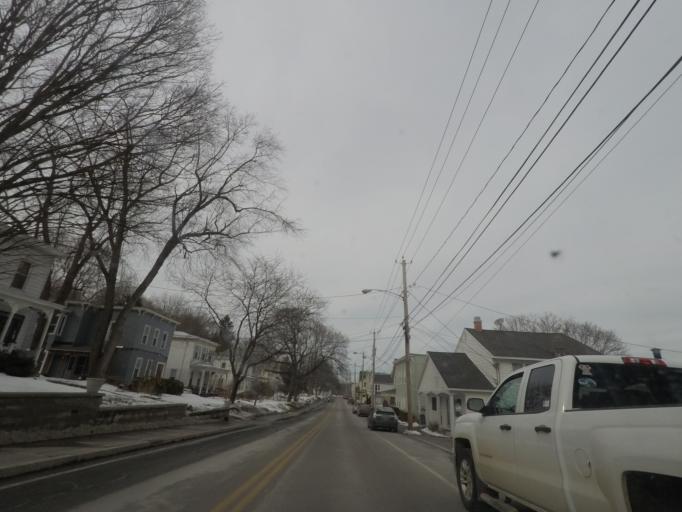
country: US
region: New York
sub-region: Albany County
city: Voorheesville
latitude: 42.6529
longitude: -73.9286
